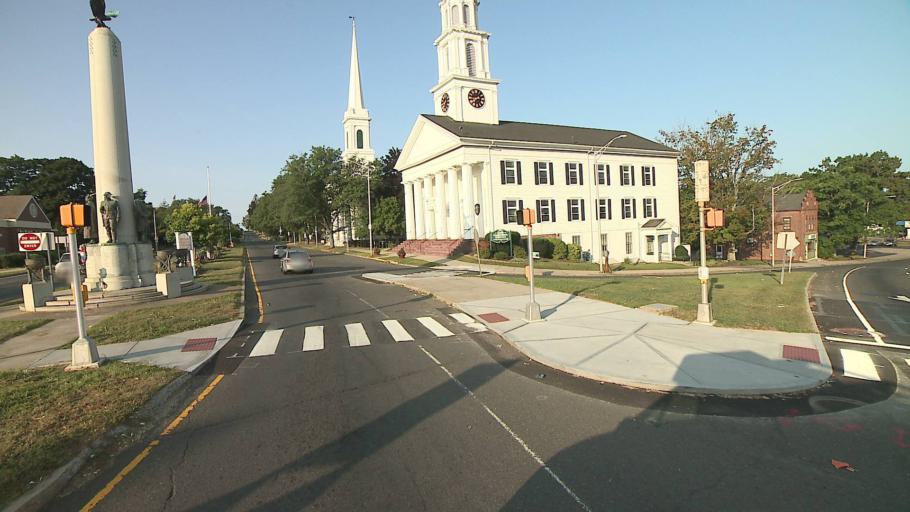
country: US
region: Connecticut
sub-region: New Haven County
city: Meriden
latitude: 41.5335
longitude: -72.7925
